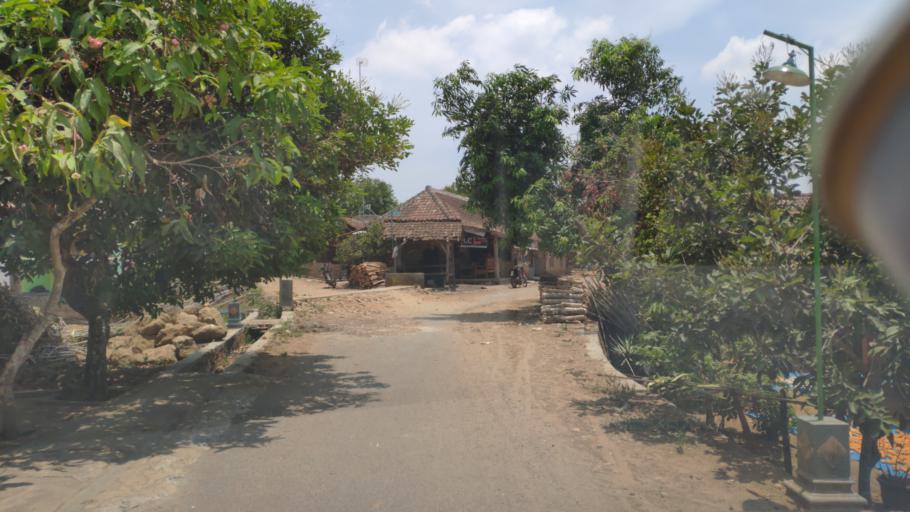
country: ID
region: Central Java
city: Ngiyono
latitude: -6.8965
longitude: 111.3112
